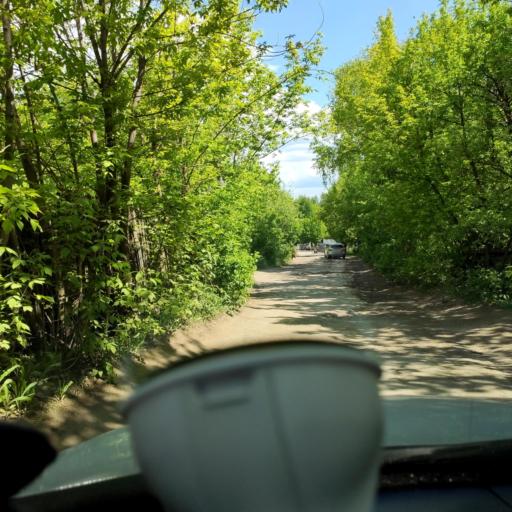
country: RU
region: Samara
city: Petra-Dubrava
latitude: 53.2740
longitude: 50.3192
